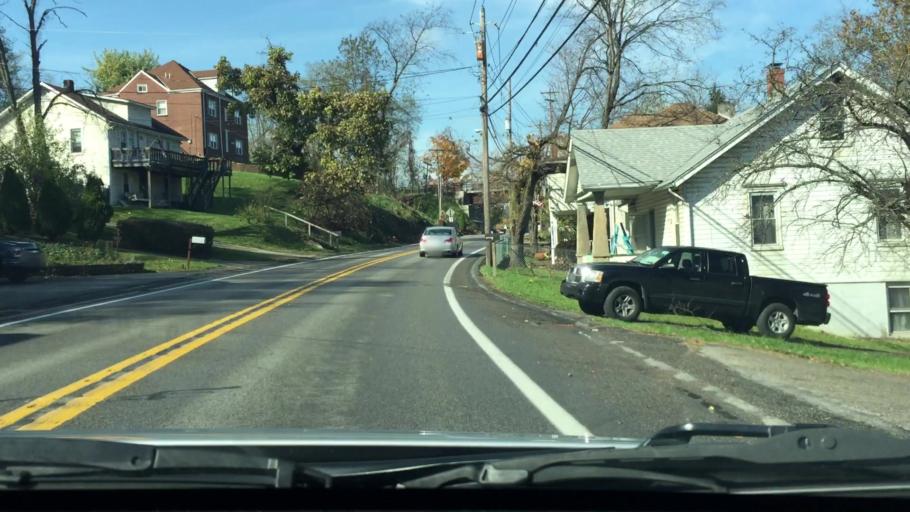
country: US
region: Pennsylvania
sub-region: Allegheny County
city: South Park Township
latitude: 40.2885
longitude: -80.0265
